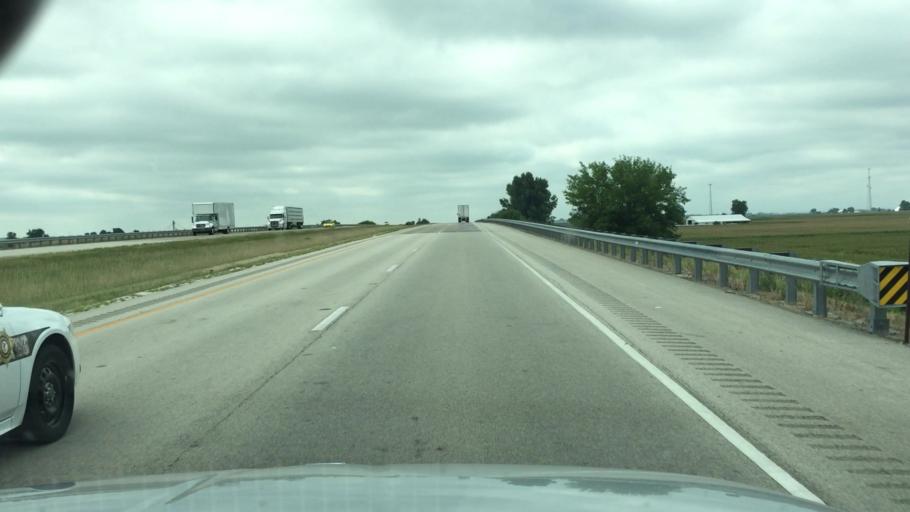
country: US
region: Illinois
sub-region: Henry County
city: Orion
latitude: 41.3521
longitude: -90.3320
